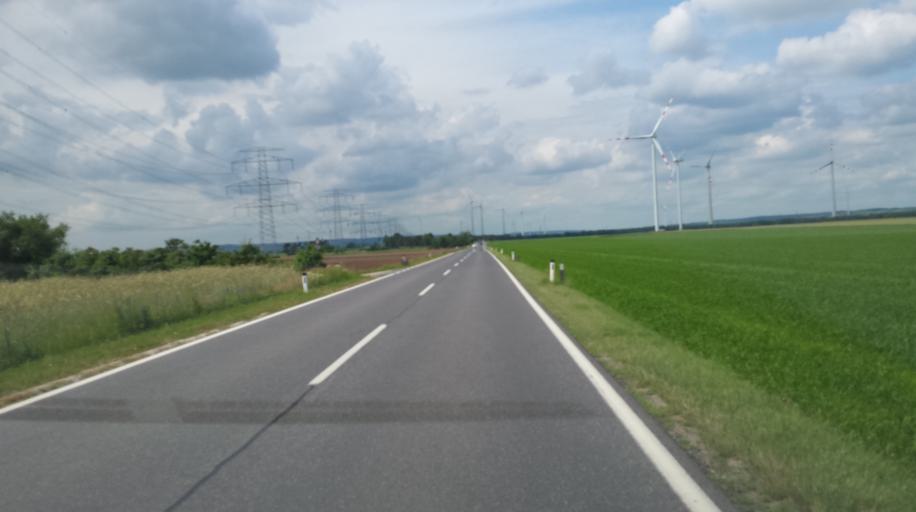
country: AT
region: Lower Austria
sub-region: Politischer Bezirk Ganserndorf
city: Aderklaa
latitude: 48.3116
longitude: 16.5359
